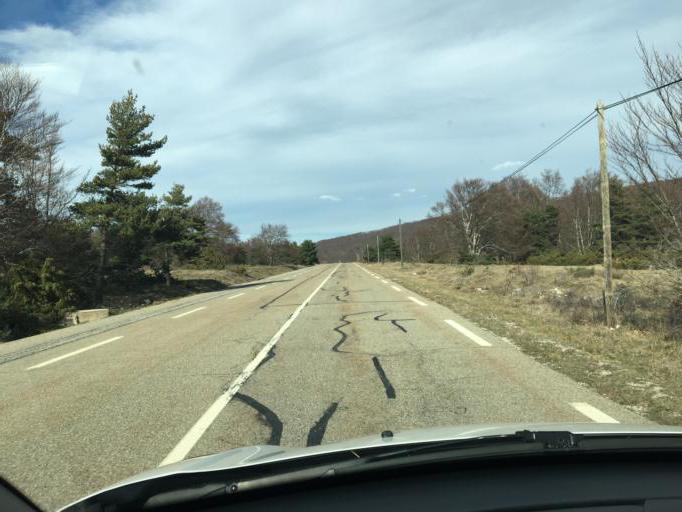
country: FR
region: Provence-Alpes-Cote d'Azur
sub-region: Departement du Vaucluse
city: Saint-Saturnin-les-Apt
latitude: 43.9774
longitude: 5.4689
